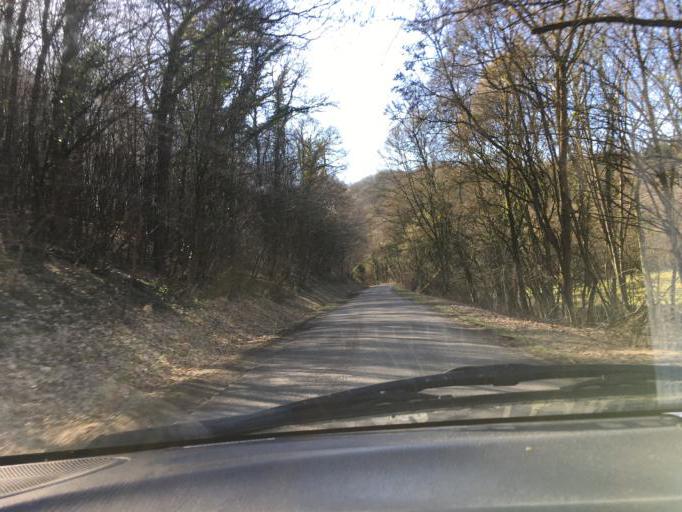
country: BE
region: Wallonia
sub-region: Province de Namur
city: Doische
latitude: 50.1312
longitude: 4.7335
